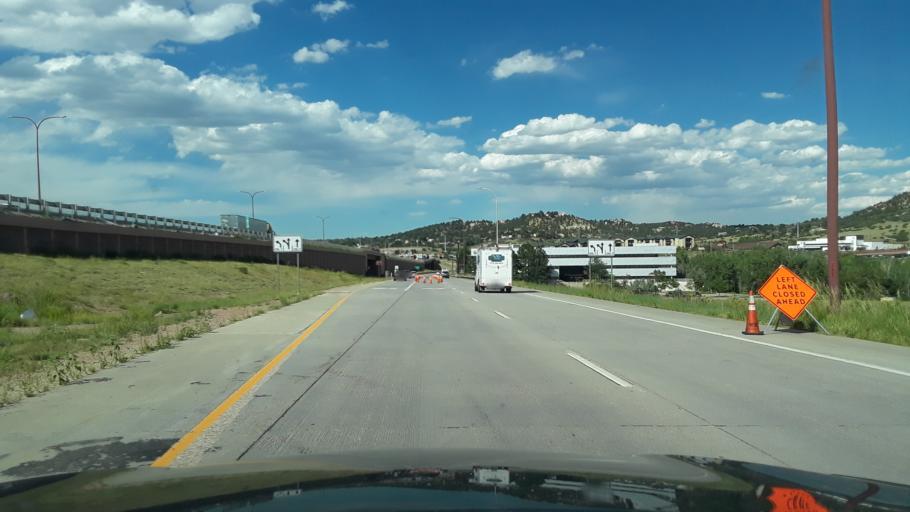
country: US
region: Colorado
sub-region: El Paso County
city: Colorado Springs
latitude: 38.9109
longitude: -104.8224
